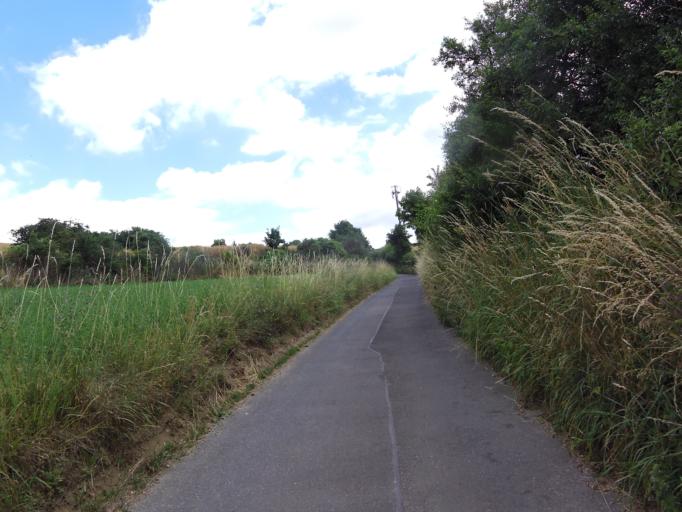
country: DE
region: Bavaria
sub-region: Regierungsbezirk Unterfranken
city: Wuerzburg
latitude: 49.7766
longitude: 9.9644
